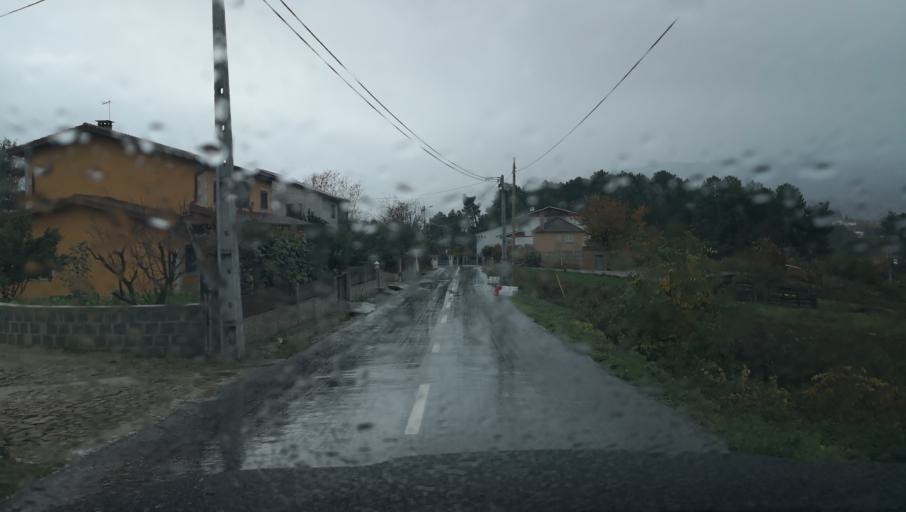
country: PT
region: Vila Real
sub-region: Vila Real
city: Vila Real
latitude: 41.2861
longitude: -7.7091
